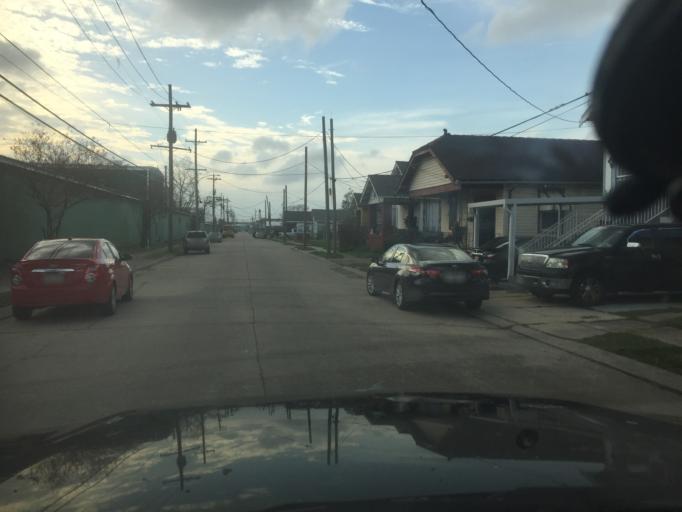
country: US
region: Louisiana
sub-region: Orleans Parish
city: New Orleans
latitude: 29.9859
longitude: -90.0790
